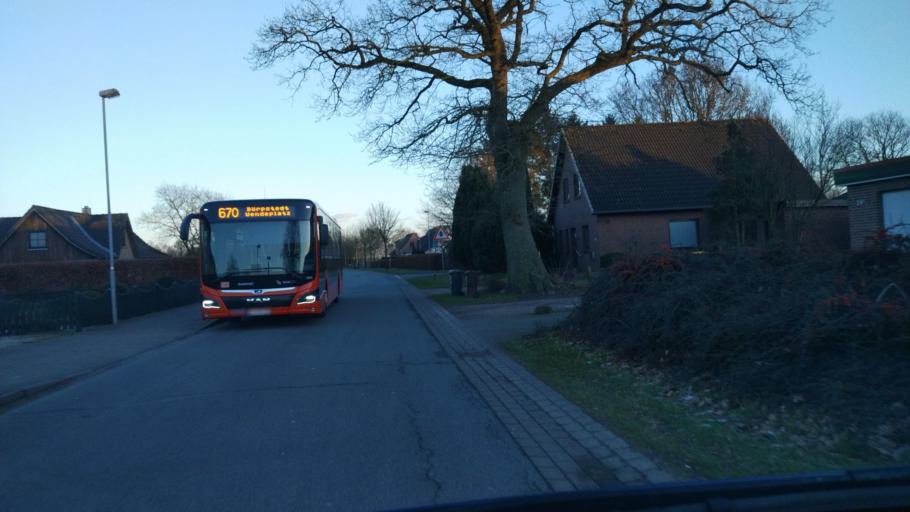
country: DE
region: Schleswig-Holstein
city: Hollingstedt
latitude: 54.4562
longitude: 9.3420
